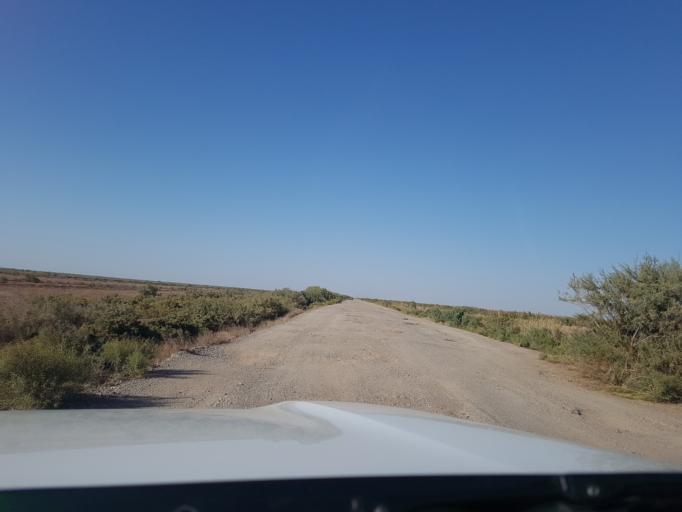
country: IR
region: Razavi Khorasan
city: Sarakhs
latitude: 36.9451
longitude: 61.3787
